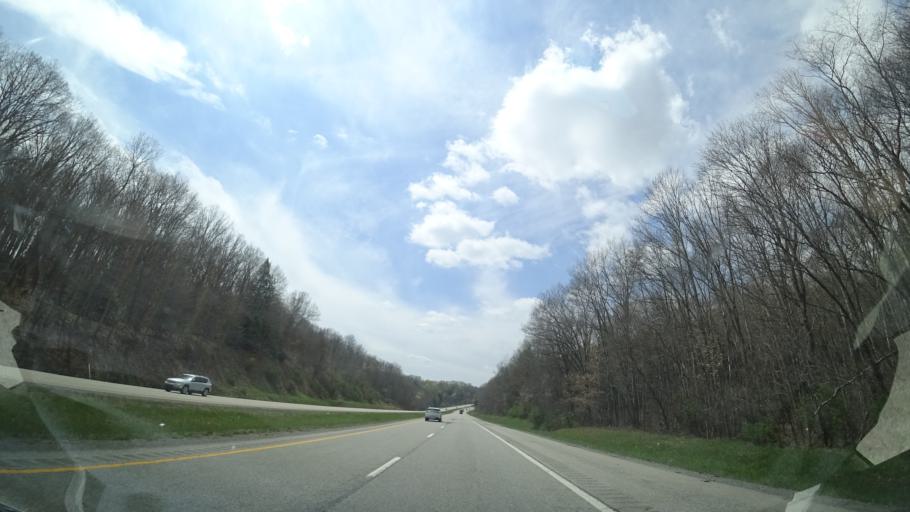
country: US
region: West Virginia
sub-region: Monongalia County
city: Cheat Lake
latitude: 39.6617
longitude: -79.6777
